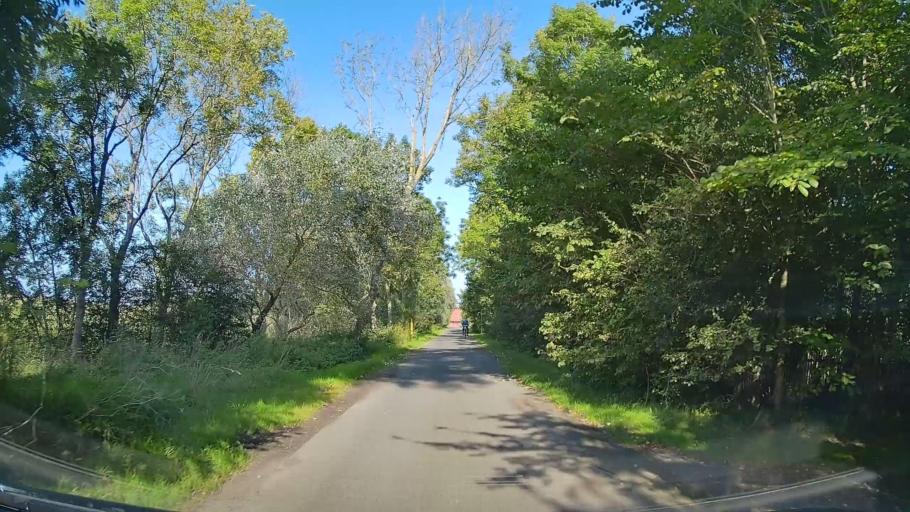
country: DE
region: Lower Saxony
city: Padingbuttel
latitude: 53.7103
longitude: 8.5088
